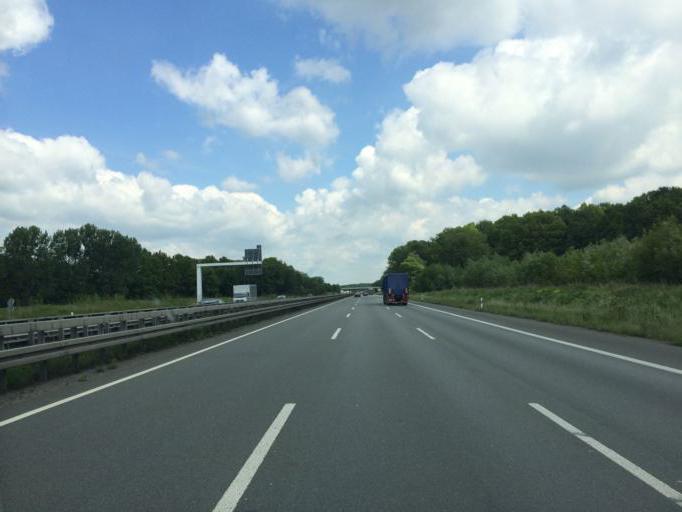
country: DE
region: North Rhine-Westphalia
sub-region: Regierungsbezirk Arnsberg
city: Welver
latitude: 51.6391
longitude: 7.8958
